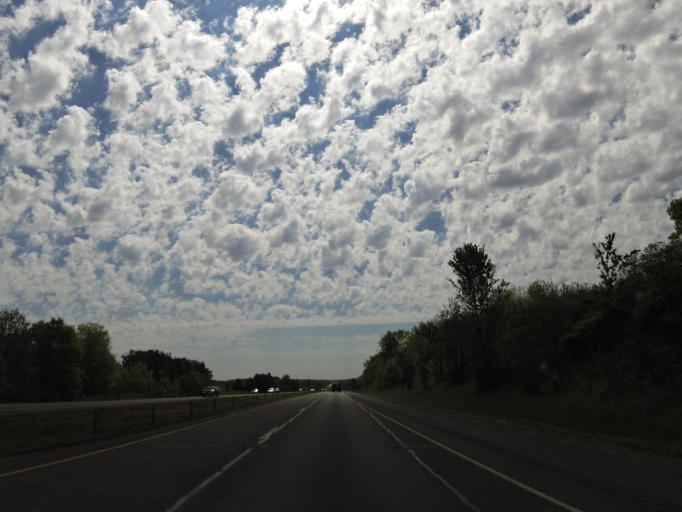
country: US
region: Wisconsin
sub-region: Dunn County
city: Colfax
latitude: 44.8830
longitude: -91.7240
